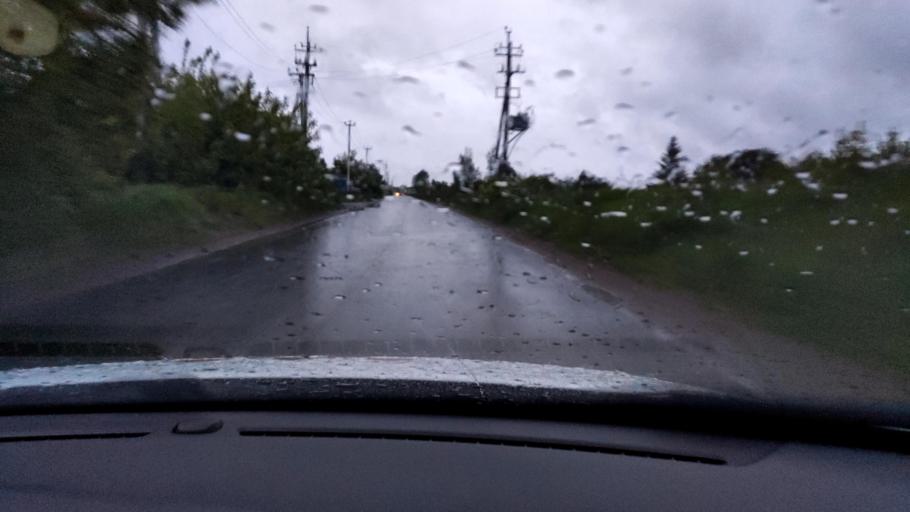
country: RU
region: Tatarstan
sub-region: Gorod Kazan'
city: Kazan
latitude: 55.7221
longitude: 49.1169
